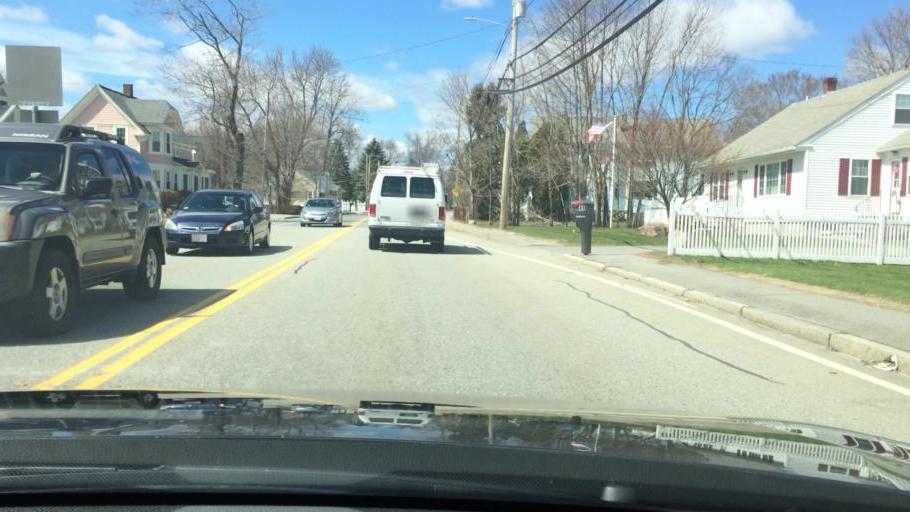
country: US
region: Massachusetts
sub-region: Essex County
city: Methuen
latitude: 42.7443
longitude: -71.1704
